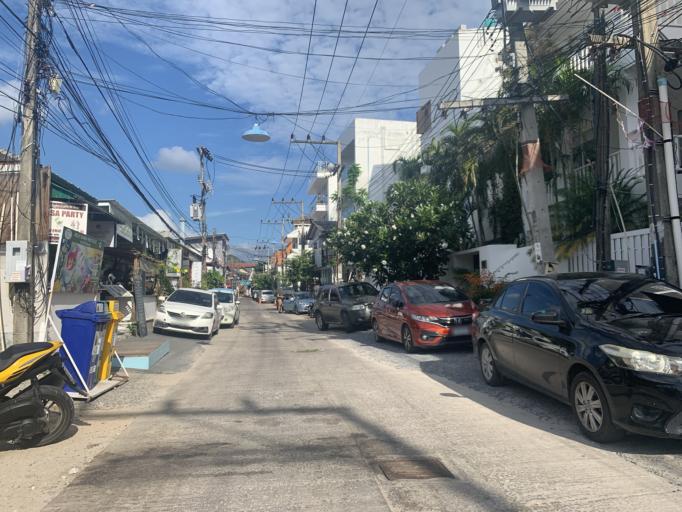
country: TH
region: Surat Thani
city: Ko Samui
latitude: 9.5595
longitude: 100.0330
